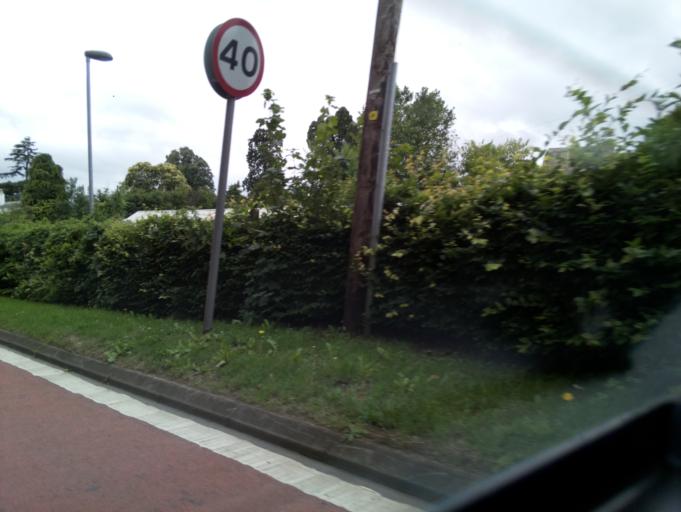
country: GB
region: England
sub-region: Gloucestershire
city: Tewkesbury
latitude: 52.0055
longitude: -2.1620
